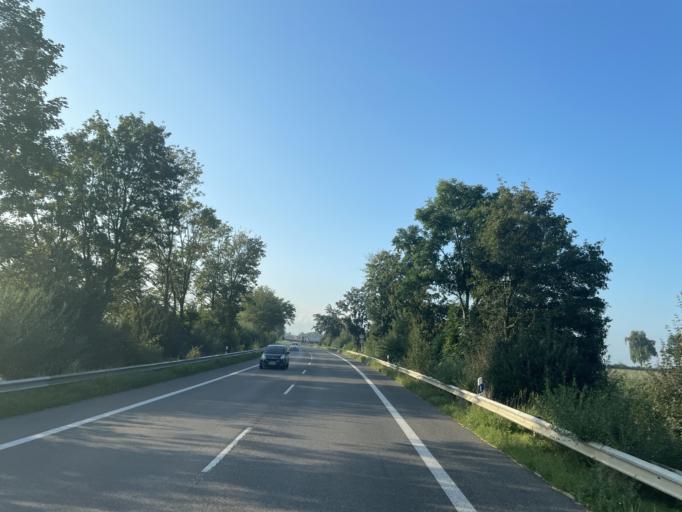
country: DE
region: North Rhine-Westphalia
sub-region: Regierungsbezirk Dusseldorf
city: Neubrueck
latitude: 51.1542
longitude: 6.5934
